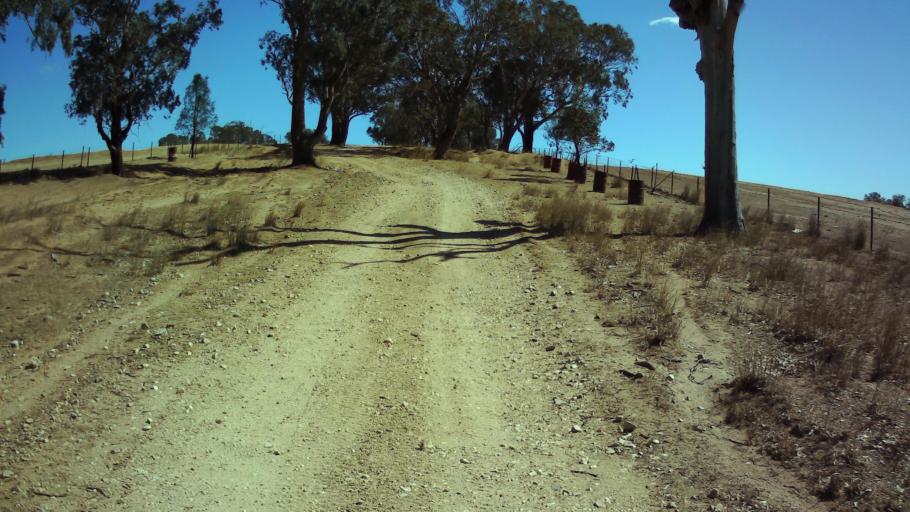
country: AU
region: New South Wales
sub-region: Weddin
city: Grenfell
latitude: -33.9995
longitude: 148.4368
